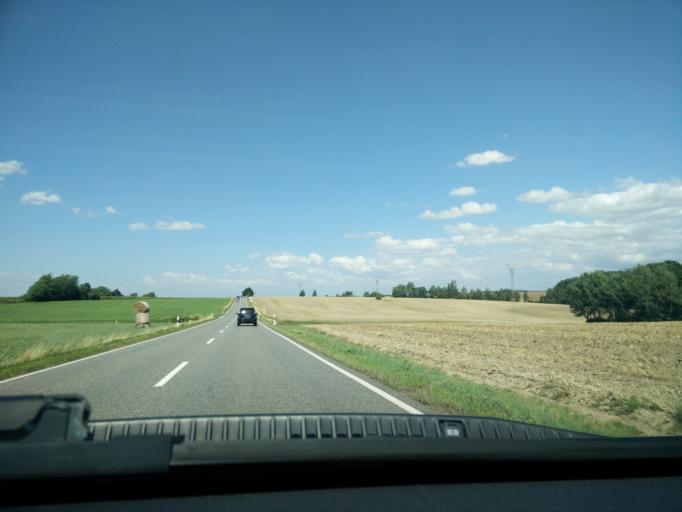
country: DE
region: Saxony
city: Narsdorf
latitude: 50.9773
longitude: 12.6978
